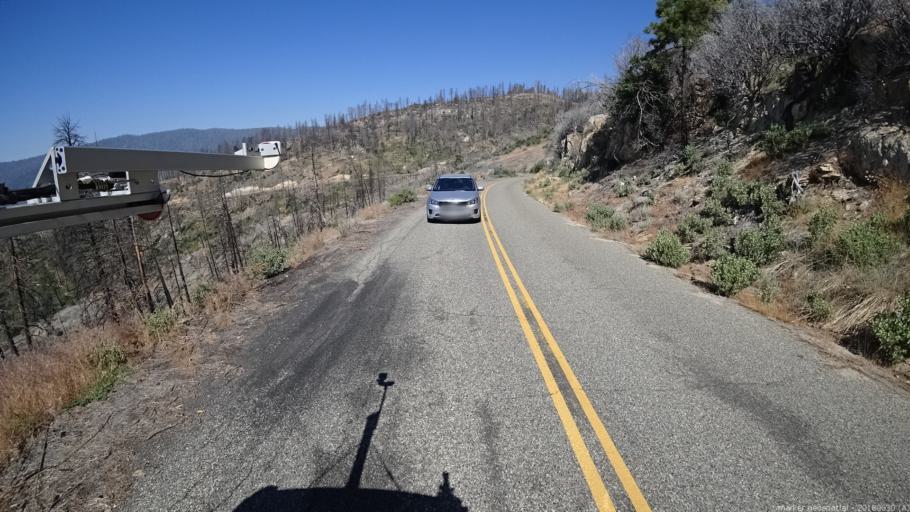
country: US
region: California
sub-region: Fresno County
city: Auberry
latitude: 37.3095
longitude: -119.3501
